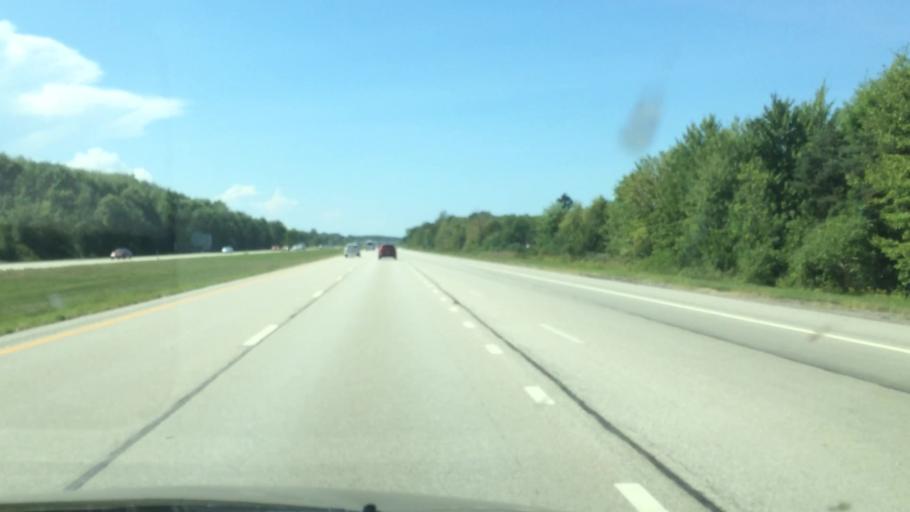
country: US
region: Ohio
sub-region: Ashtabula County
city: Conneaut
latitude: 41.9162
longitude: -80.5741
